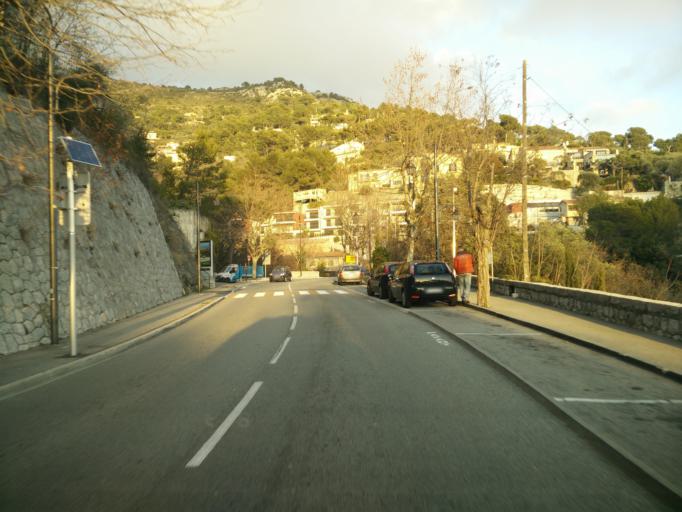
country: FR
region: Provence-Alpes-Cote d'Azur
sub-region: Departement des Alpes-Maritimes
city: Eze
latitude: 43.7309
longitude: 7.3635
